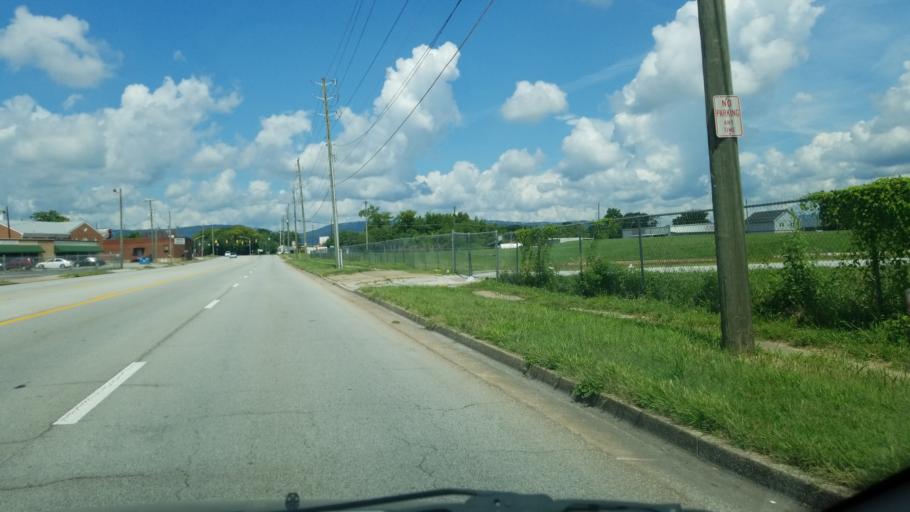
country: US
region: Tennessee
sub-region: Hamilton County
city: Chattanooga
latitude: 35.0235
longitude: -85.2950
